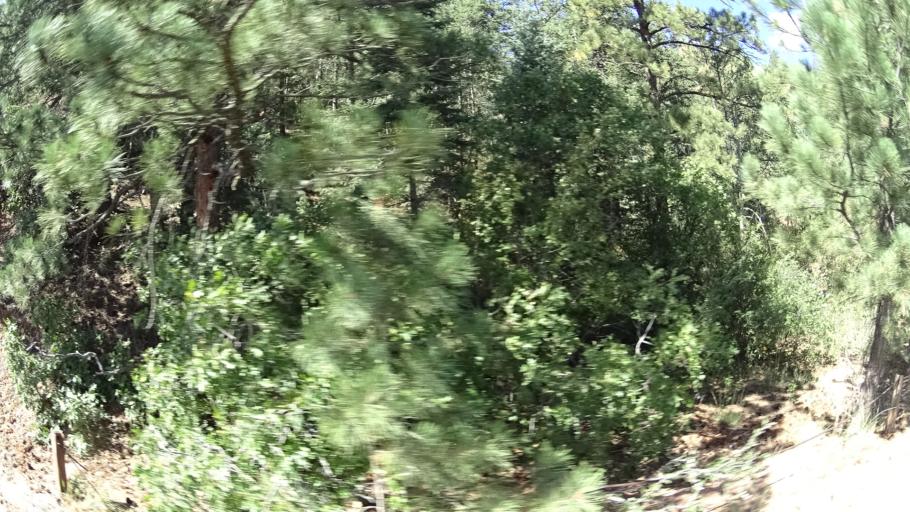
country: US
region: Colorado
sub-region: El Paso County
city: Colorado Springs
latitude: 38.8026
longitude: -104.8774
